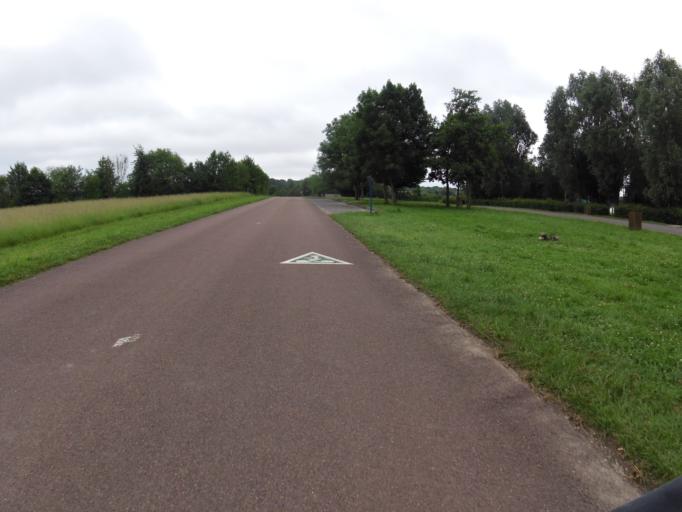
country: FR
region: Champagne-Ardenne
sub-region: Departement de la Haute-Marne
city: Montier-en-Der
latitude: 48.5523
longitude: 4.7935
